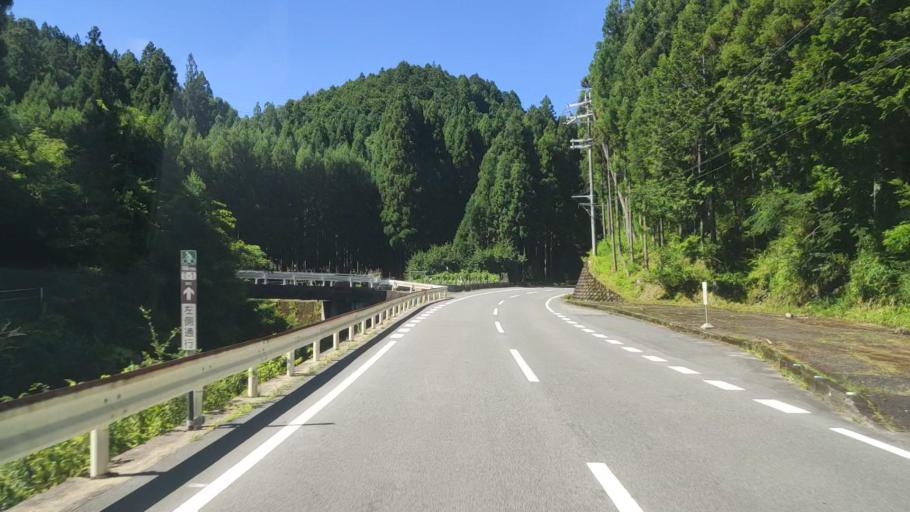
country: JP
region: Nara
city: Yoshino-cho
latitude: 34.4153
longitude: 135.9348
